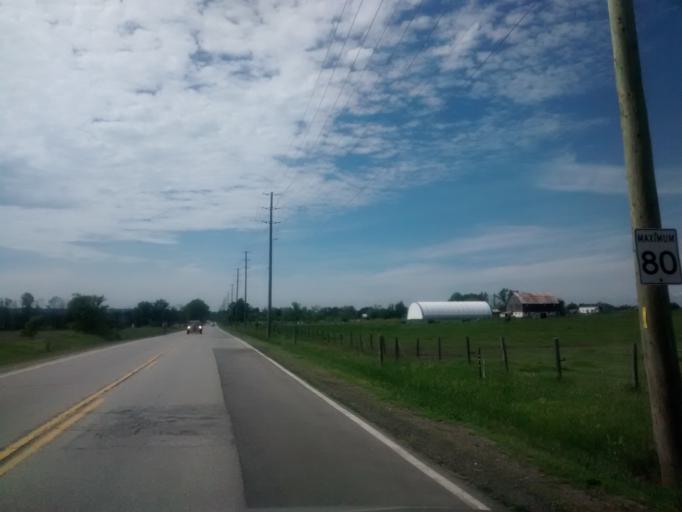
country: CA
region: Ontario
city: Burlington
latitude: 43.4420
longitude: -79.8208
